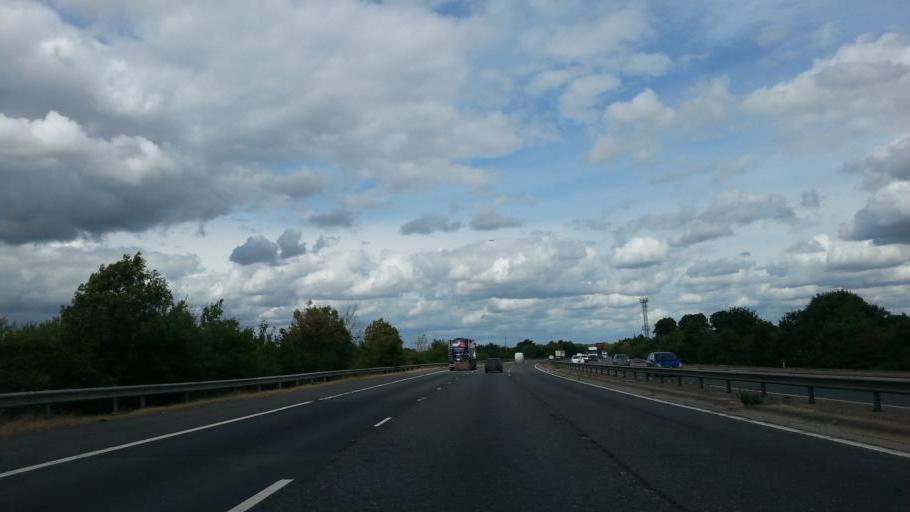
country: GB
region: England
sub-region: Essex
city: Little Hallingbury
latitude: 51.8207
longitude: 0.1849
